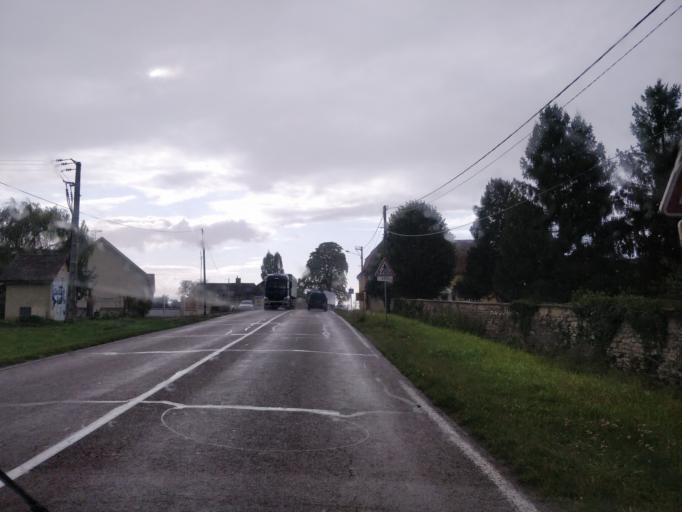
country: FR
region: Champagne-Ardenne
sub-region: Departement de l'Aube
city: Lusigny-sur-Barse
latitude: 48.2395
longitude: 4.2999
